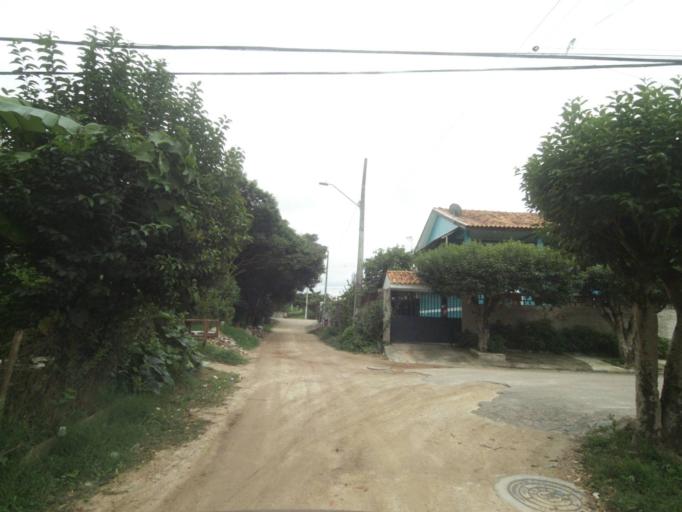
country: BR
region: Parana
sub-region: Pinhais
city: Pinhais
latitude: -25.4532
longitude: -49.1998
